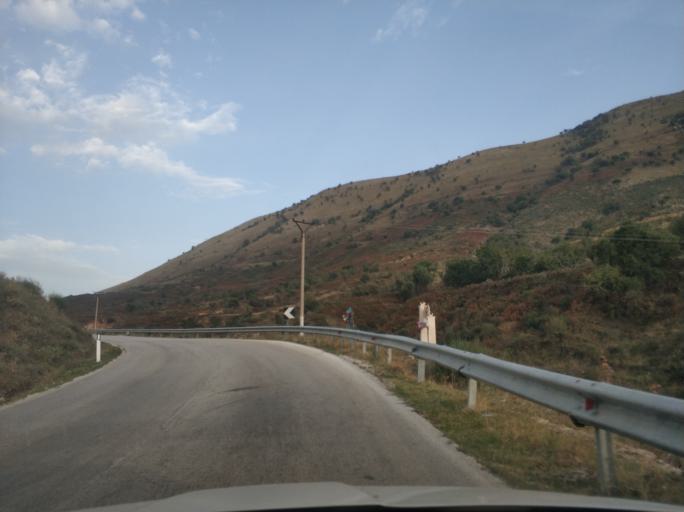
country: AL
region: Gjirokaster
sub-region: Rrethi i Gjirokastres
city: Libohove
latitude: 39.9375
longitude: 20.2171
